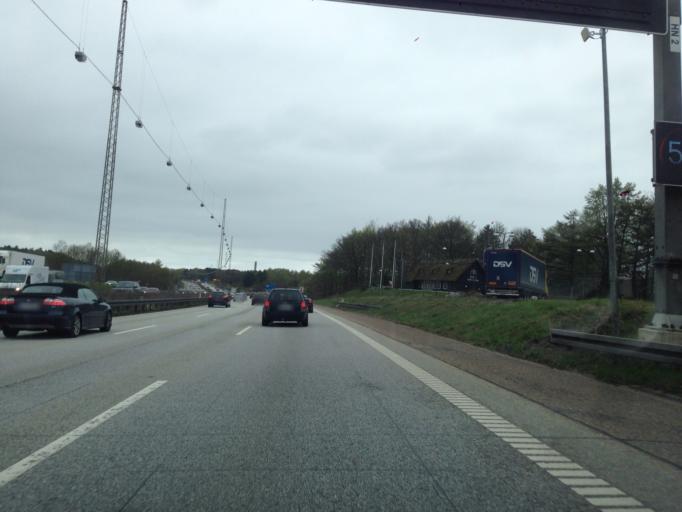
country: DK
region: Capital Region
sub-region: Lyngby-Tarbaek Kommune
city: Kongens Lyngby
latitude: 55.7990
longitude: 12.5333
